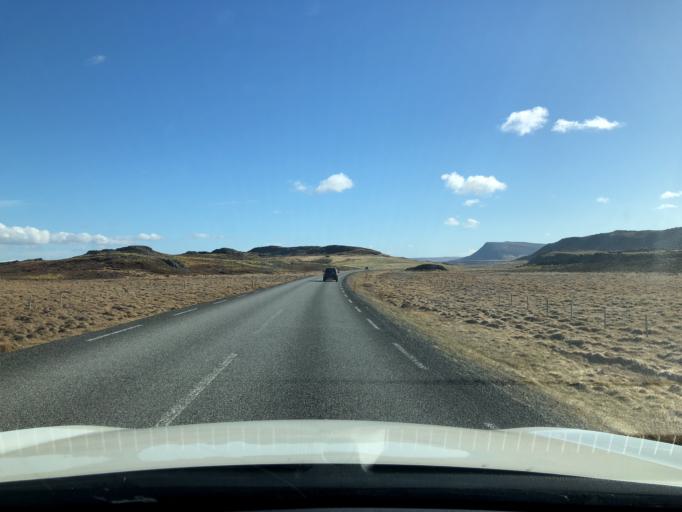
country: IS
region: West
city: Borgarnes
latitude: 64.5689
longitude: -21.6833
